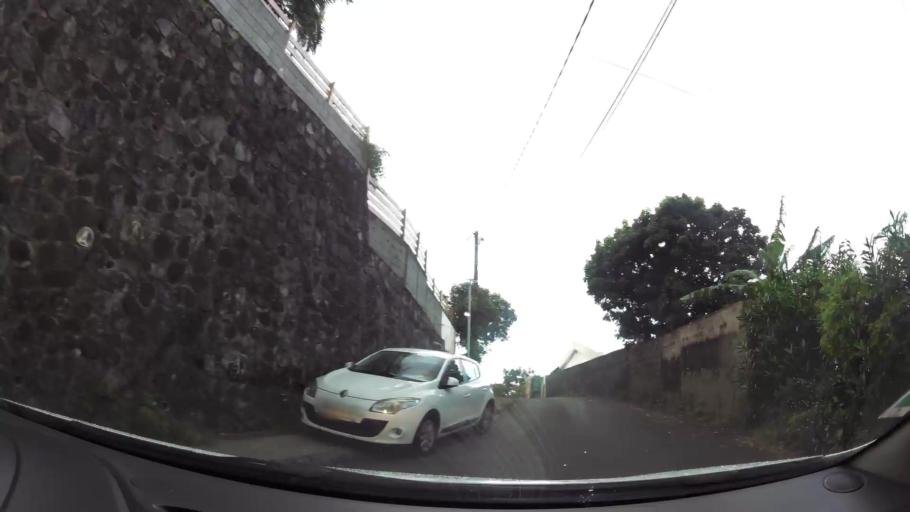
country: RE
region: Reunion
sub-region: Reunion
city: Saint-Denis
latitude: -20.9055
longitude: 55.4458
